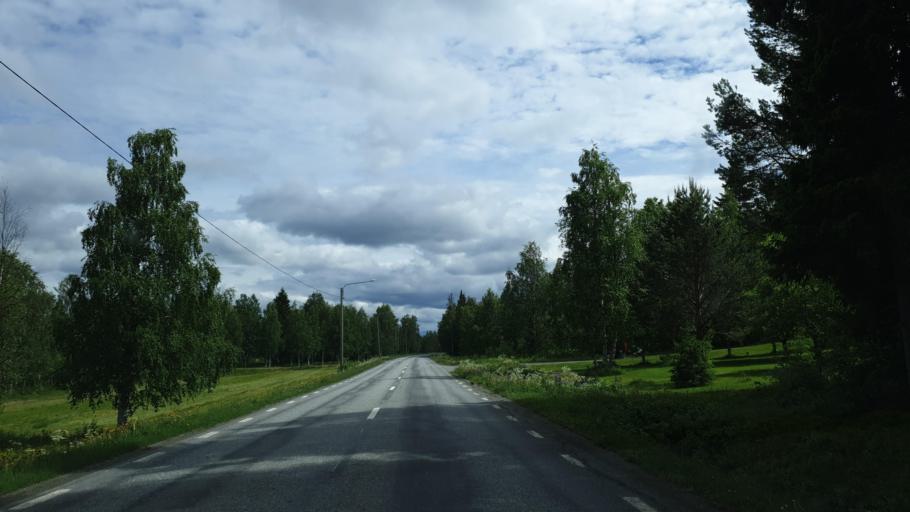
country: SE
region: Vaesterbotten
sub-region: Vilhelmina Kommun
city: Sjoberg
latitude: 64.6473
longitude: 16.3446
